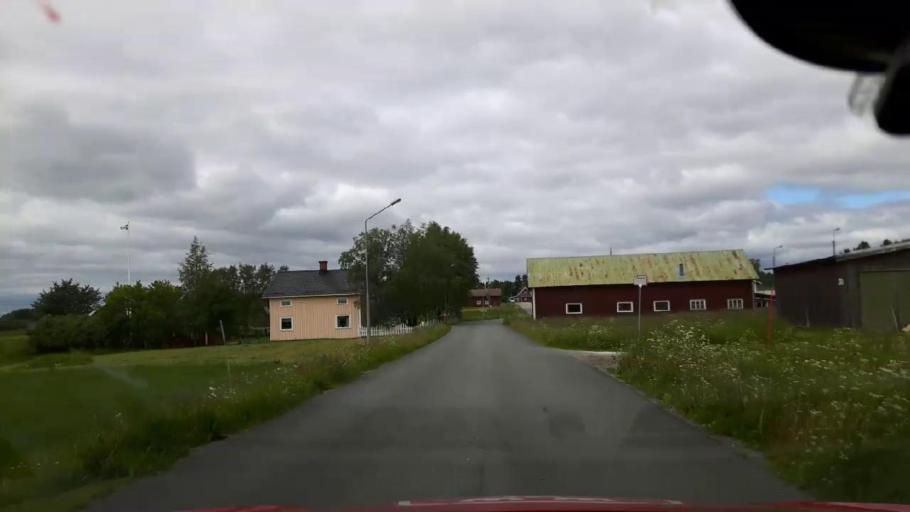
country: SE
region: Jaemtland
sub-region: OEstersunds Kommun
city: Brunflo
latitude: 63.0787
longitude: 14.8752
